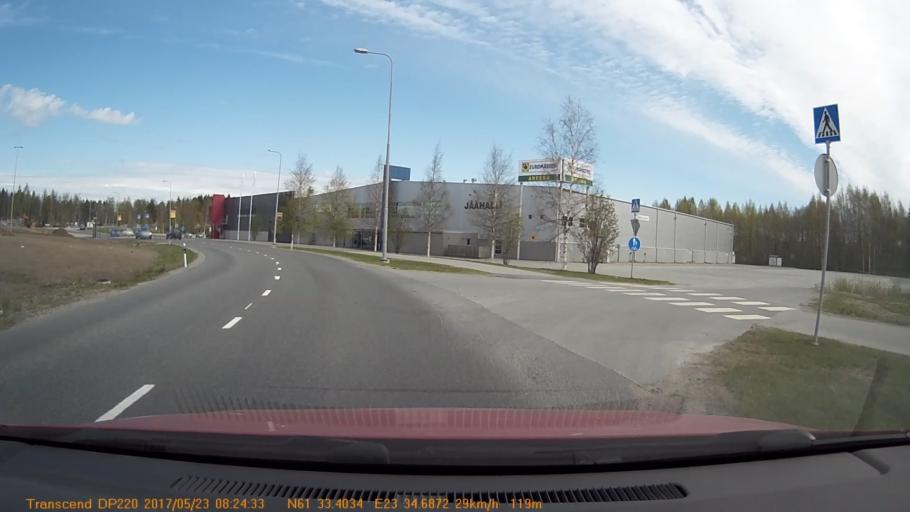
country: FI
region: Pirkanmaa
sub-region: Tampere
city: Yloejaervi
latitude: 61.5568
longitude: 23.5781
